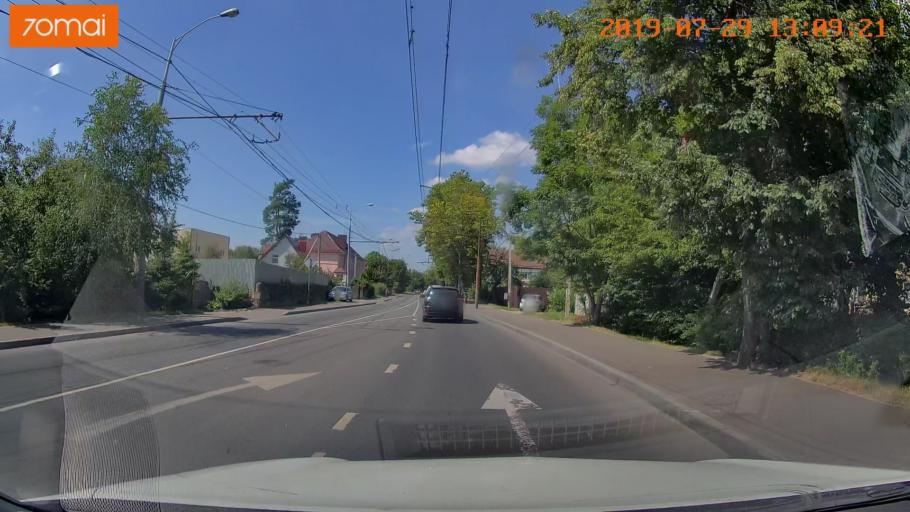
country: RU
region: Kaliningrad
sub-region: Gorod Kaliningrad
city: Kaliningrad
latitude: 54.7136
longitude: 20.4187
